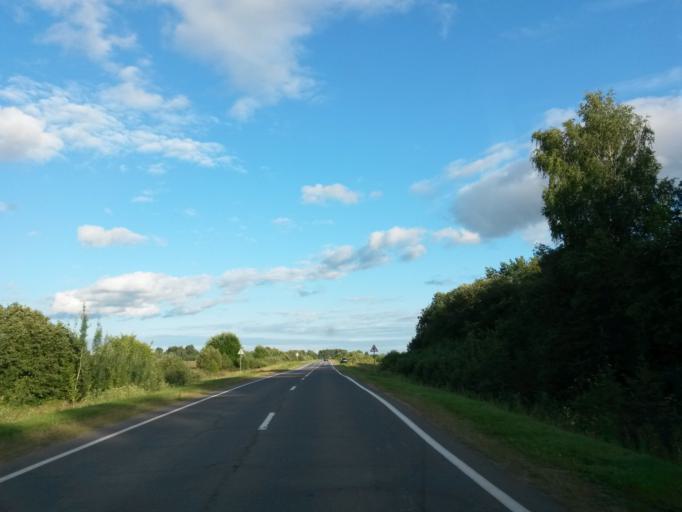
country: RU
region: Jaroslavl
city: Konstantinovskiy
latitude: 57.8528
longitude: 39.6237
